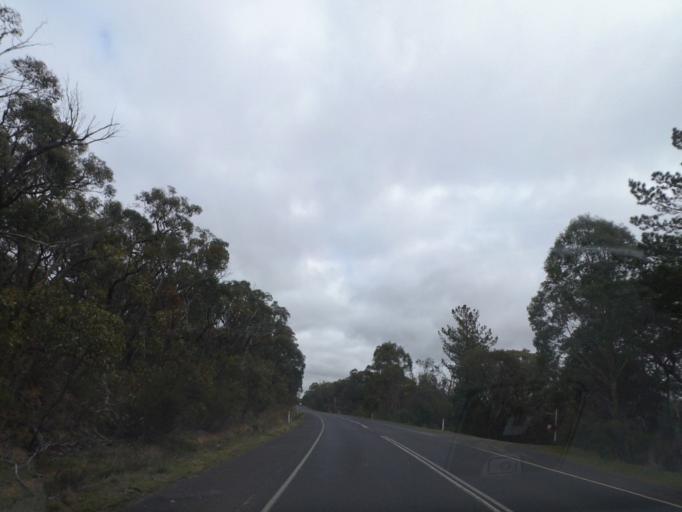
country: AU
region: Victoria
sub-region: Whittlesea
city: Whittlesea
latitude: -37.4183
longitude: 145.0452
